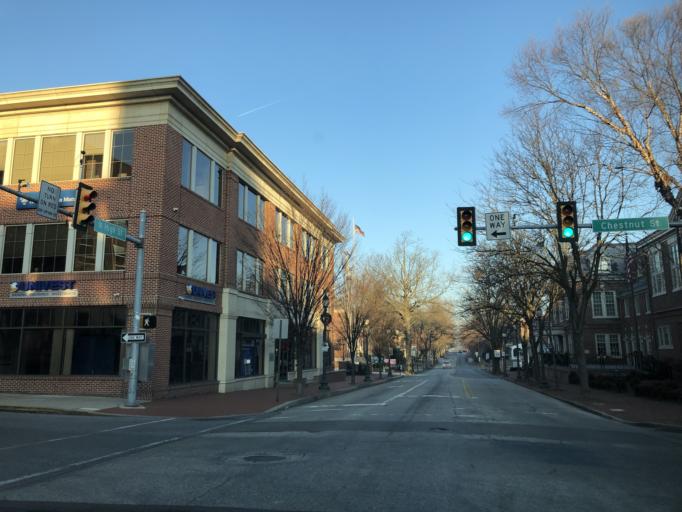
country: US
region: Pennsylvania
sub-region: Chester County
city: West Chester
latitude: 39.9613
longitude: -75.6059
